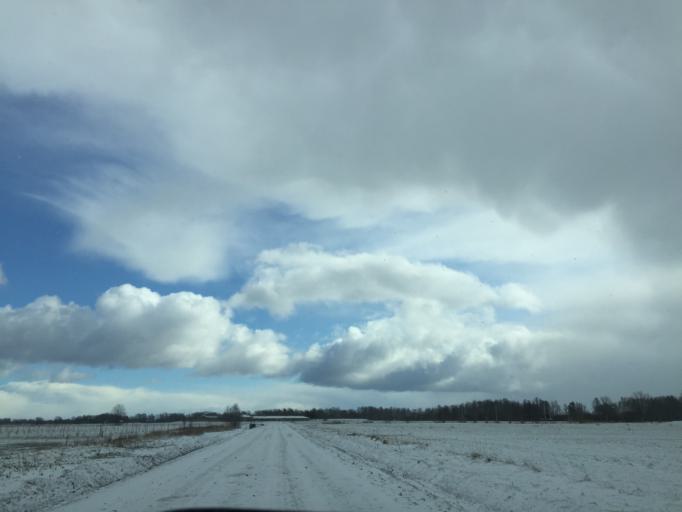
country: LV
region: Ventspils
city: Ventspils
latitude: 57.3736
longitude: 21.6226
